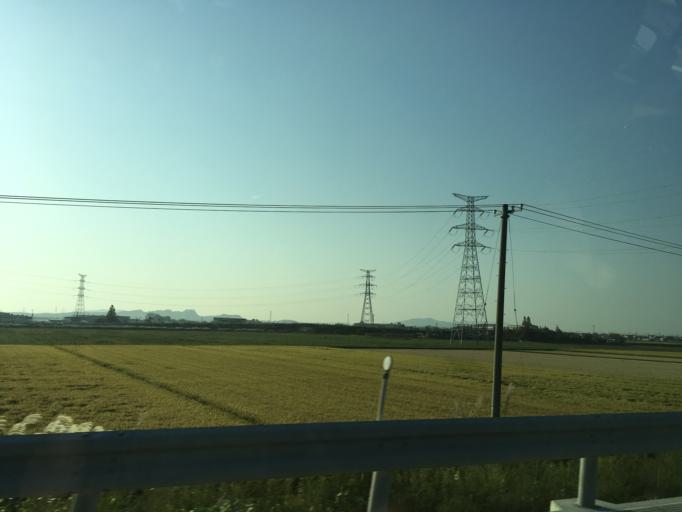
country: JP
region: Miyagi
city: Ishinomaki
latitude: 38.4787
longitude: 141.2922
